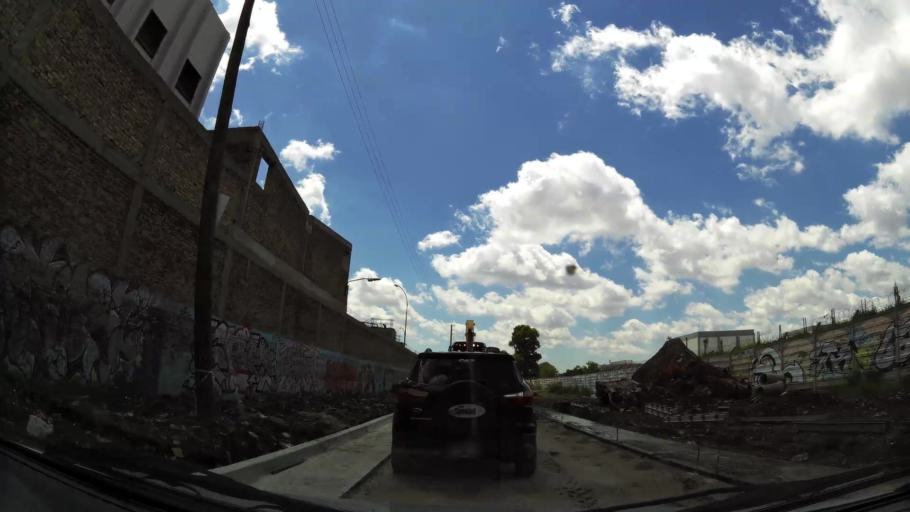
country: AR
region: Buenos Aires F.D.
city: Villa Lugano
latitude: -34.6873
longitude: -58.4408
